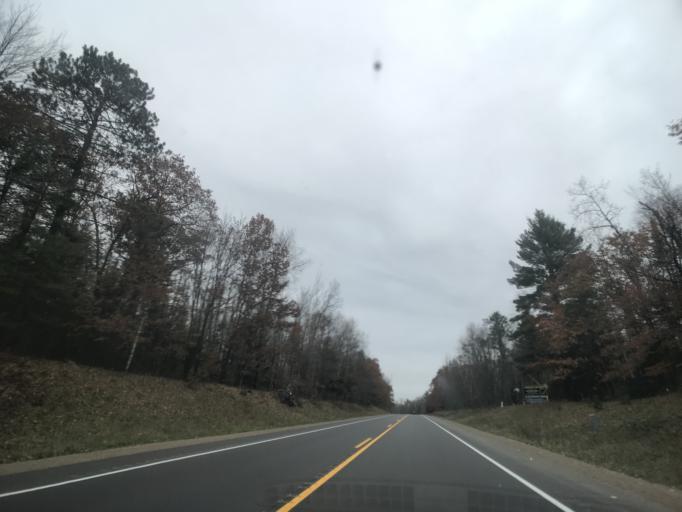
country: US
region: Wisconsin
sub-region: Menominee County
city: Legend Lake
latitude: 45.2678
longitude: -88.5109
